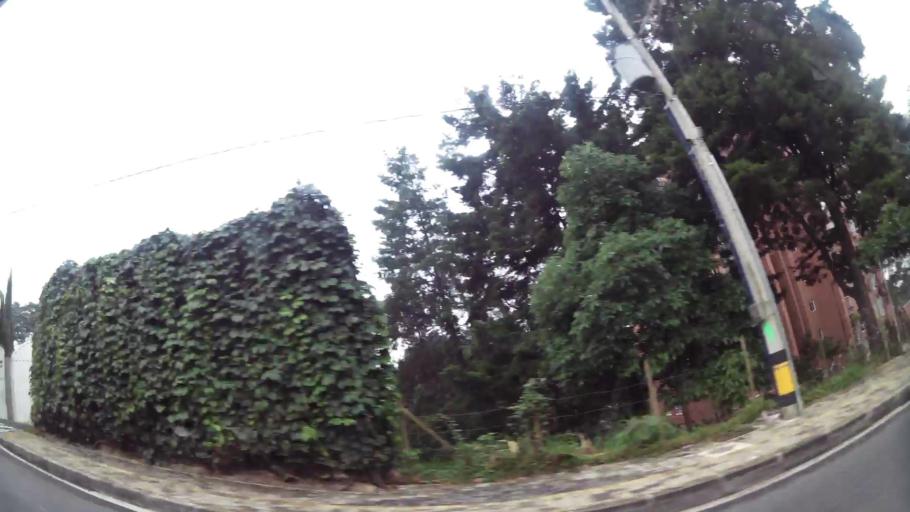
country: CO
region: Antioquia
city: Envigado
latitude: 6.1870
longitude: -75.5634
